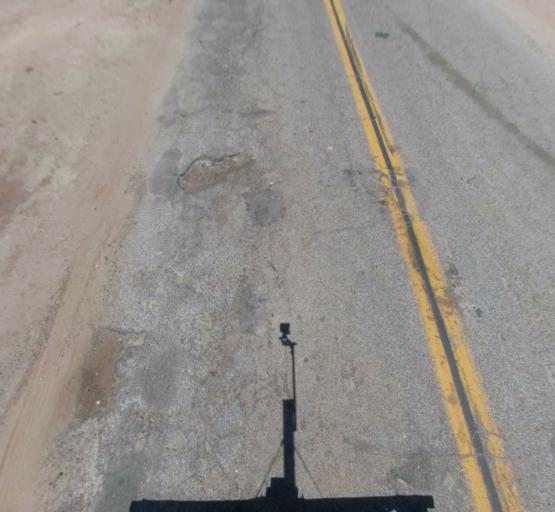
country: US
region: California
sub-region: Madera County
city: Parkwood
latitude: 36.8513
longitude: -120.1103
